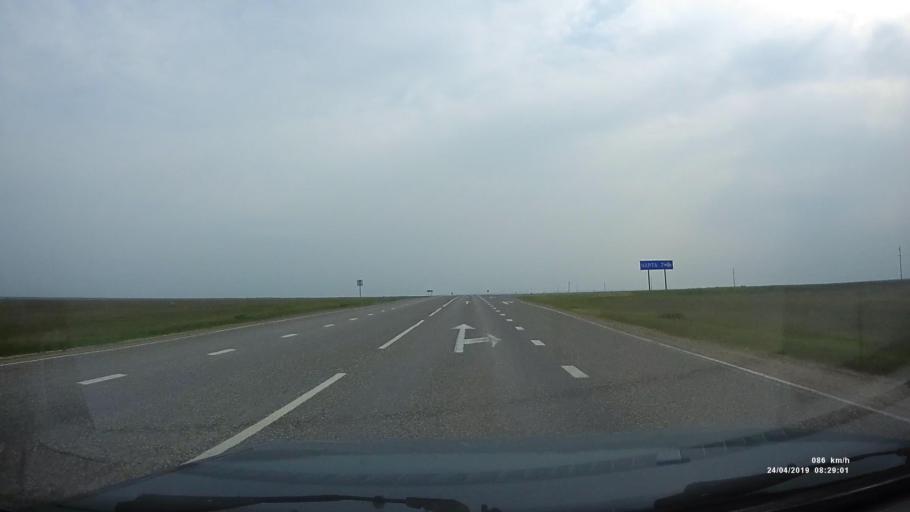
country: RU
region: Kalmykiya
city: Priyutnoye
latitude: 46.1490
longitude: 43.8246
